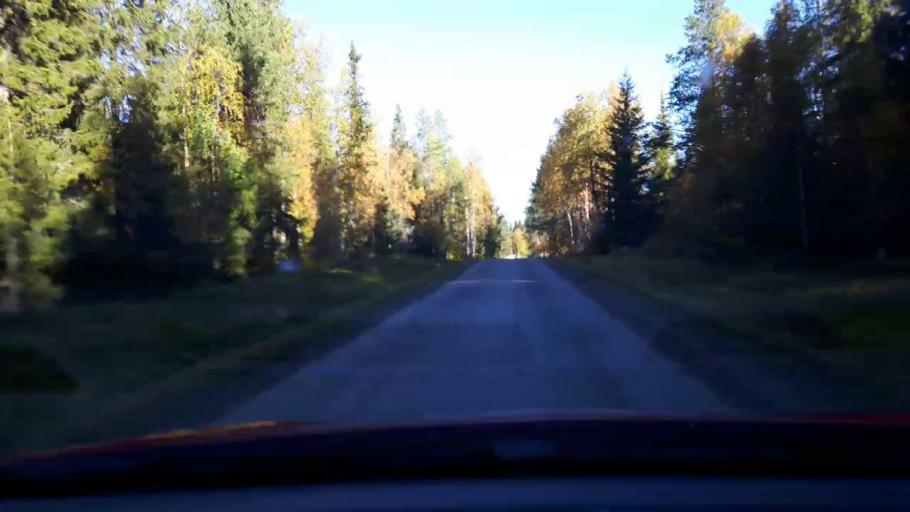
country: SE
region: Jaemtland
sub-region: Stroemsunds Kommun
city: Stroemsund
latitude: 64.3963
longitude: 15.1466
